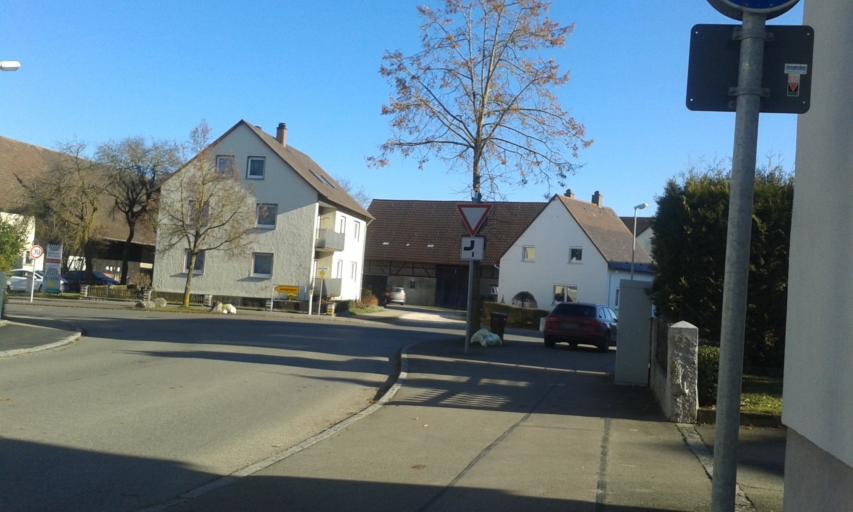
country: DE
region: Baden-Wuerttemberg
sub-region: Tuebingen Region
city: Ulm
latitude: 48.4323
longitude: 9.9684
